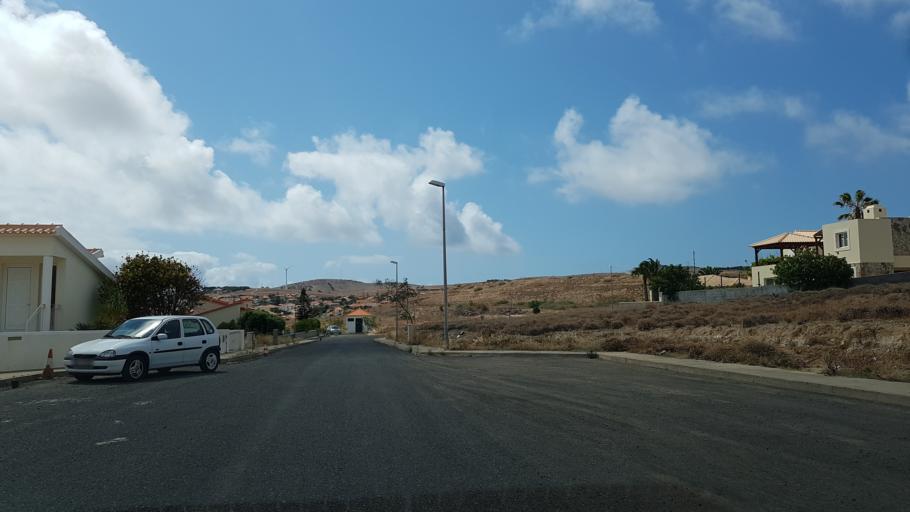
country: PT
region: Madeira
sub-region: Porto Santo
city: Vila de Porto Santo
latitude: 33.0543
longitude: -16.3458
